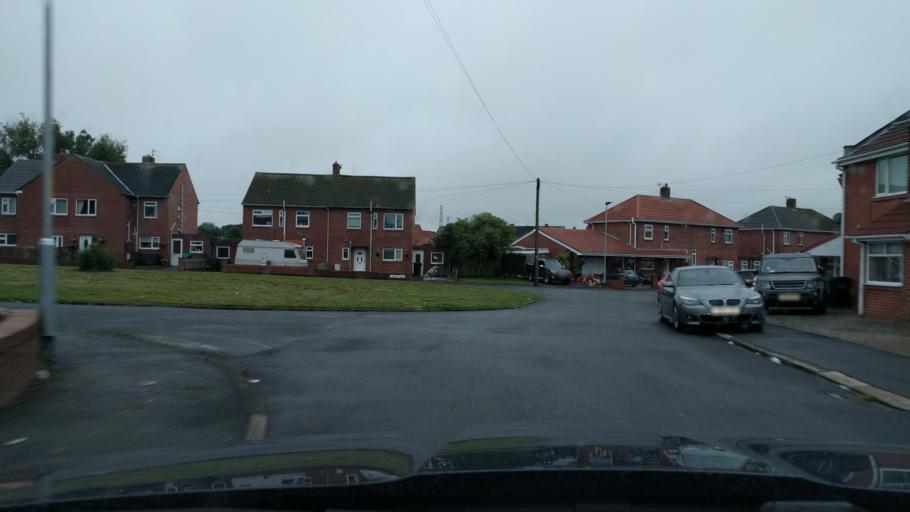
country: GB
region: England
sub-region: Northumberland
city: Bedlington
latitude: 55.1361
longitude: -1.5706
